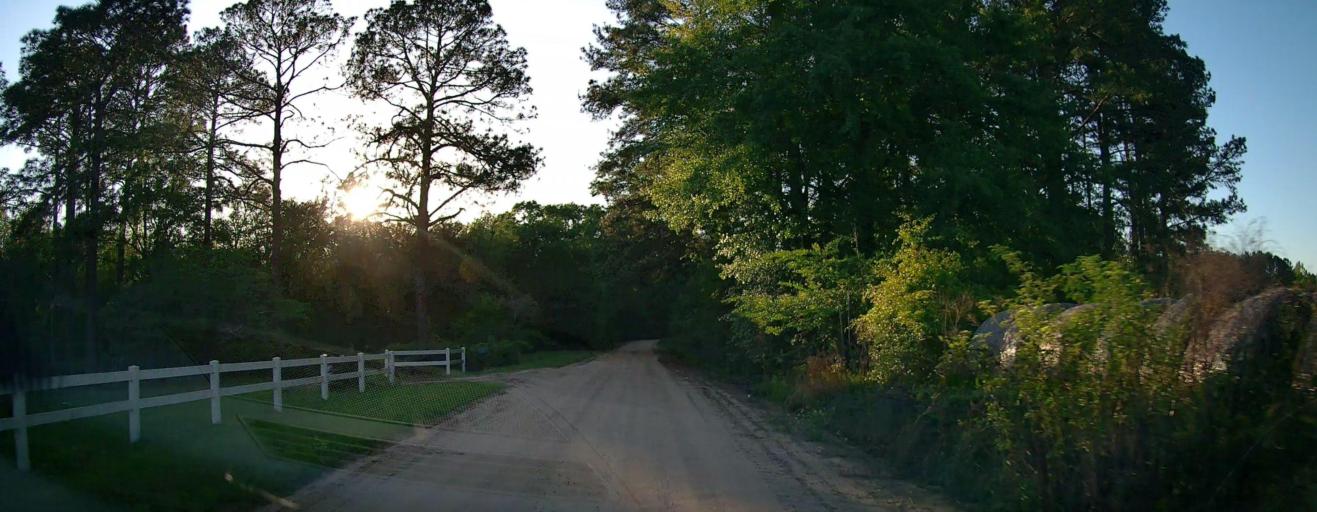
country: US
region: Georgia
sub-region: Irwin County
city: Ocilla
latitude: 31.6505
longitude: -83.2290
